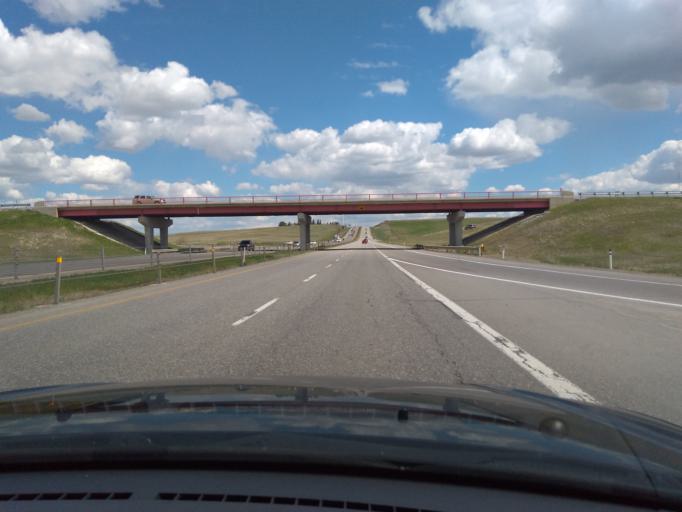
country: CA
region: Alberta
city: Cochrane
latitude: 51.0884
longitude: -114.3049
